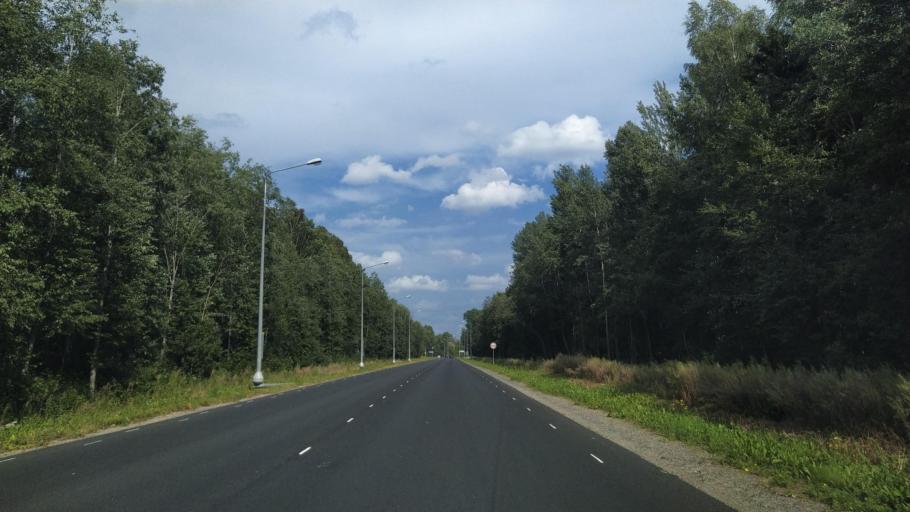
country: RU
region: Pskov
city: Vybor
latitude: 57.7290
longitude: 28.9682
